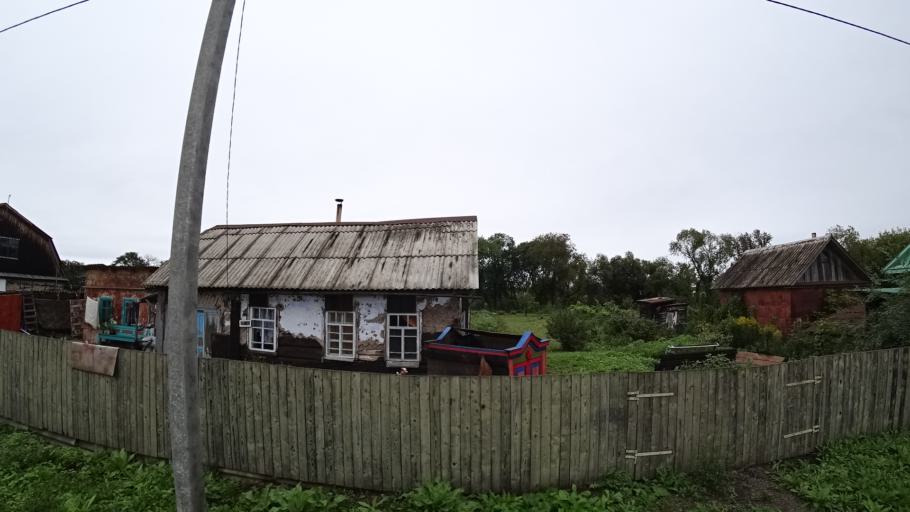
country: RU
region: Primorskiy
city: Monastyrishche
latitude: 44.2035
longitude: 132.4249
